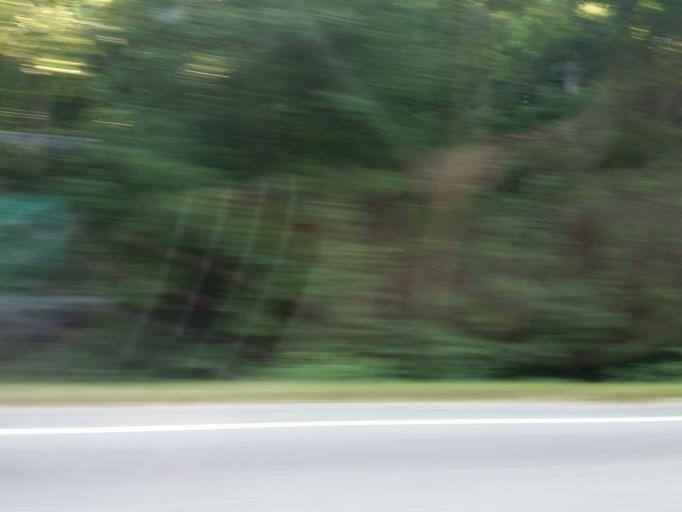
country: US
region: Tennessee
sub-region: Maury County
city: Mount Pleasant
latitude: 35.5741
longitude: -87.3229
